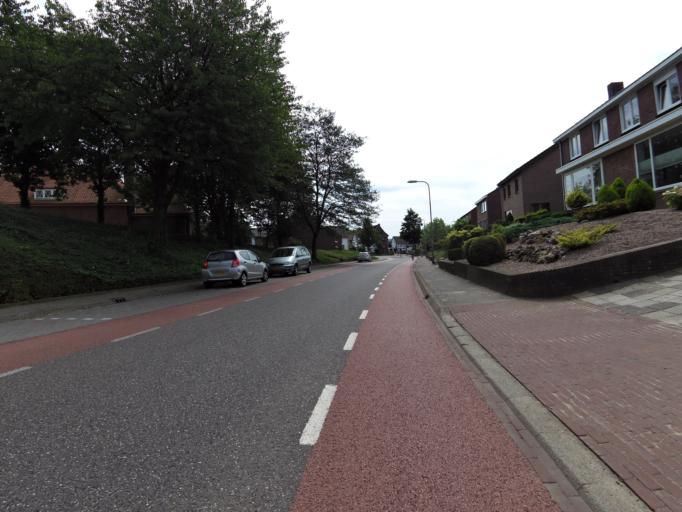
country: NL
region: Limburg
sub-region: Gemeente Voerendaal
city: Ubachsberg
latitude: 50.7978
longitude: 5.9278
